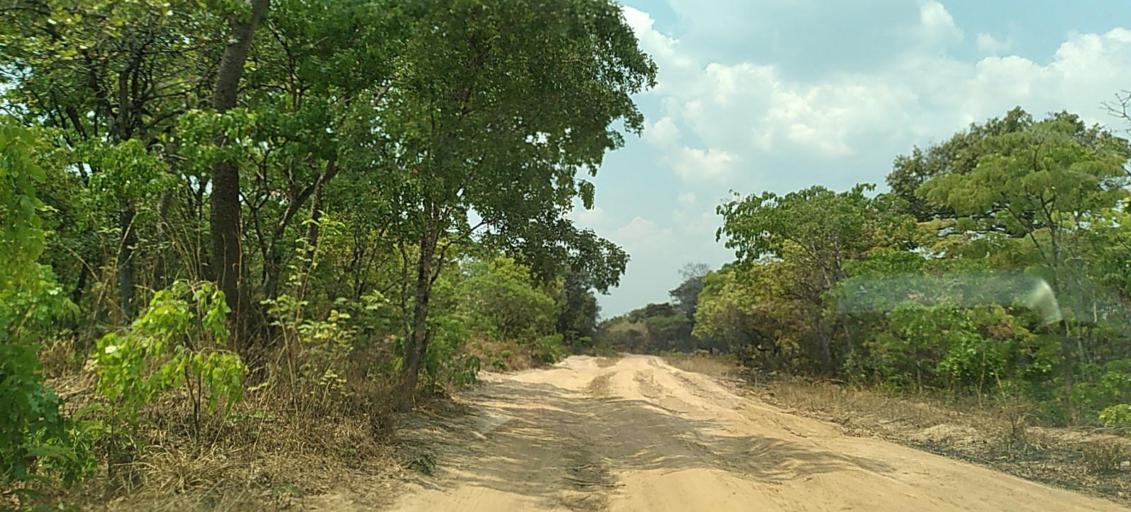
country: ZM
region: Copperbelt
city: Chingola
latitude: -12.6838
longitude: 27.7209
